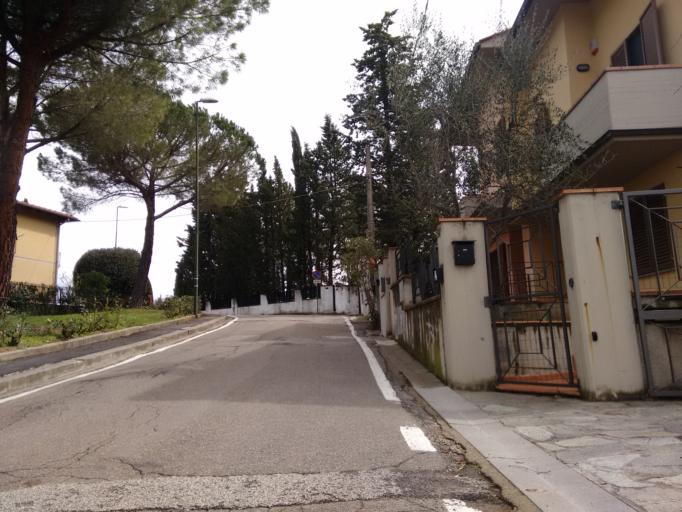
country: IT
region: Tuscany
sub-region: Province of Florence
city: Strada in Chianti
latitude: 43.6568
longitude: 11.3054
